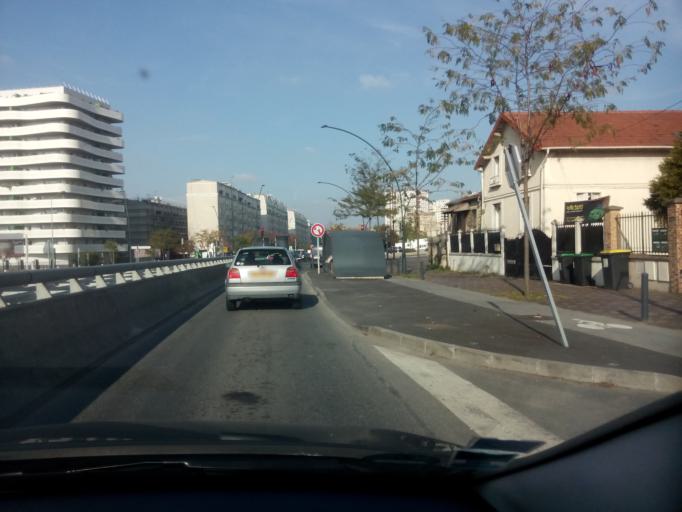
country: FR
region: Ile-de-France
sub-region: Departement du Val-de-Marne
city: Gentilly
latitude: 48.8044
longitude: 2.3444
